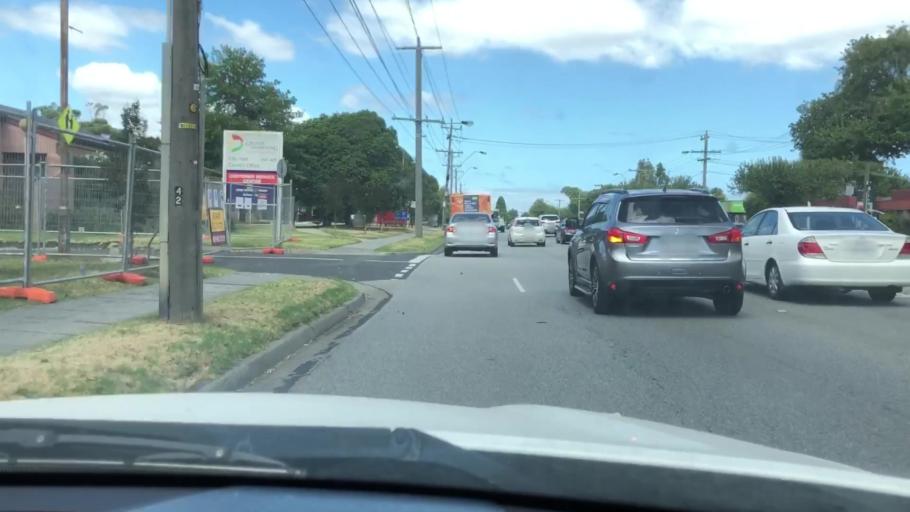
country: AU
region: Victoria
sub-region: Greater Dandenong
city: Springvale
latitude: -37.9557
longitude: 145.1517
